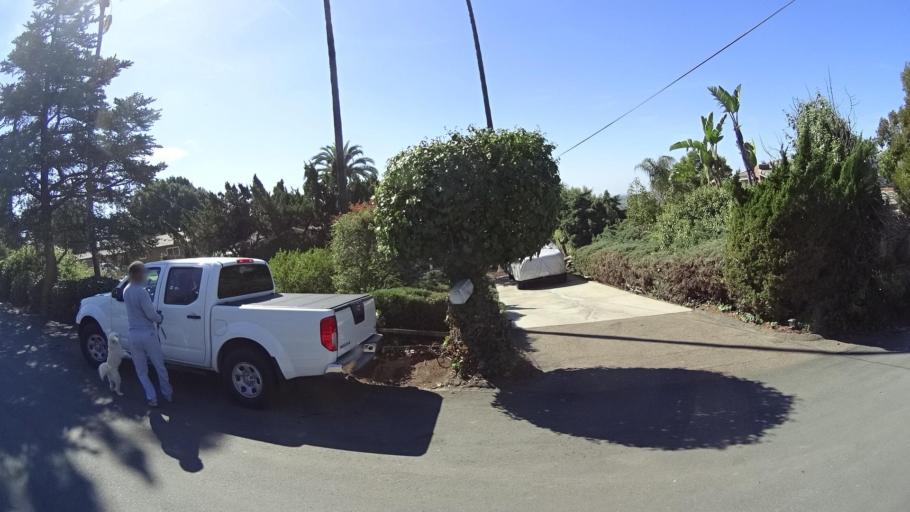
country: US
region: California
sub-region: San Diego County
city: Casa de Oro-Mount Helix
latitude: 32.7487
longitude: -116.9688
